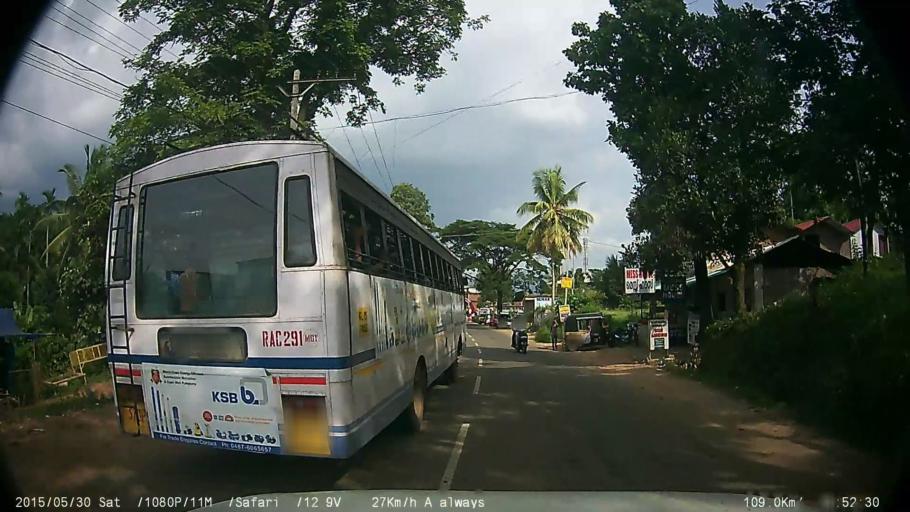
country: IN
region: Kerala
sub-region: Wayanad
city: Panamaram
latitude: 11.6773
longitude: 76.0748
